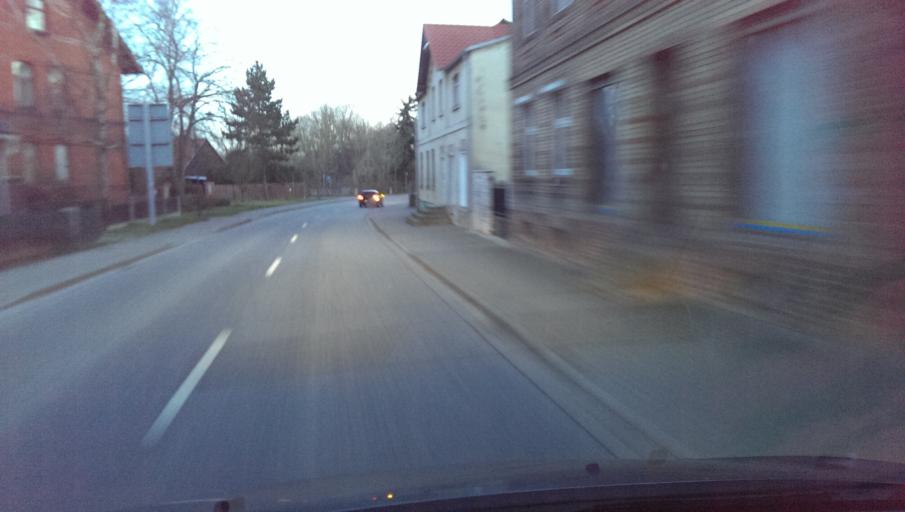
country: DE
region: Saxony-Anhalt
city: Ausleben
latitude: 52.0390
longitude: 11.0953
